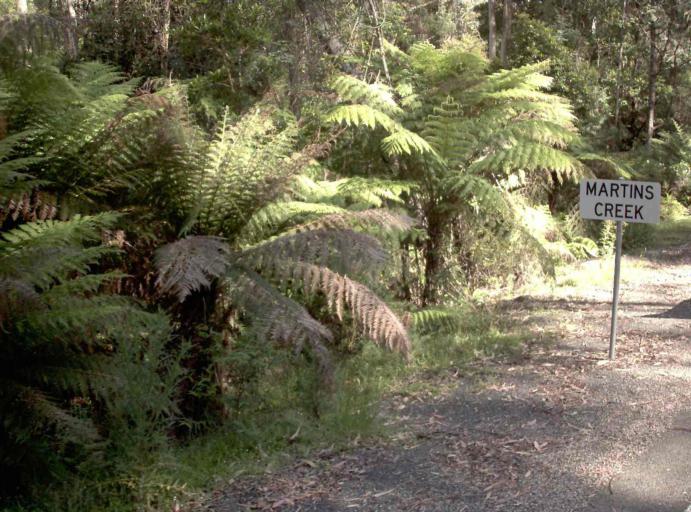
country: AU
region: Victoria
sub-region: East Gippsland
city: Lakes Entrance
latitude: -37.4180
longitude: 148.6031
